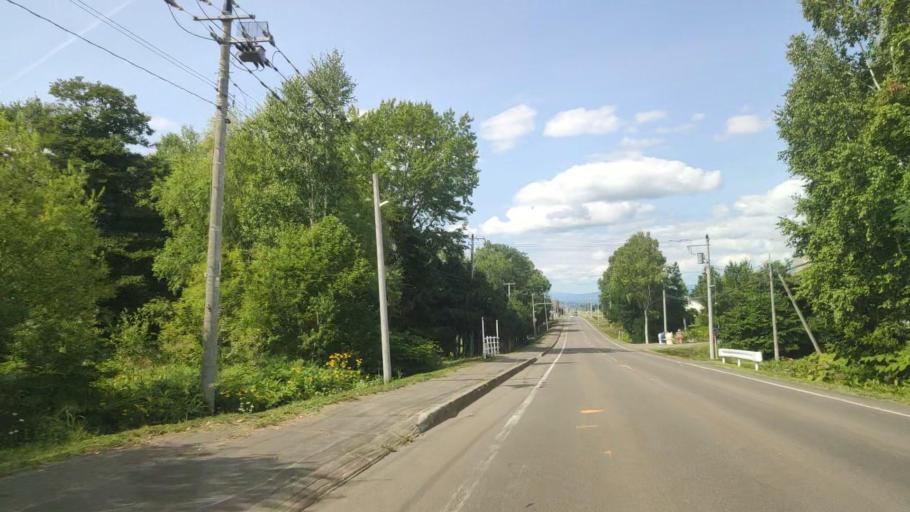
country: JP
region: Hokkaido
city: Nayoro
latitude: 44.2865
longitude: 142.4295
